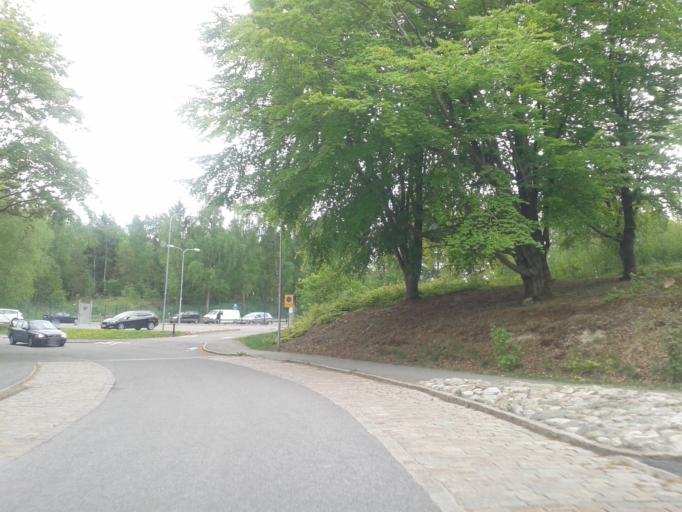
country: SE
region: Vaestra Goetaland
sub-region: Kungalvs Kommun
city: Kungalv
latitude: 57.8688
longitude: 11.9913
